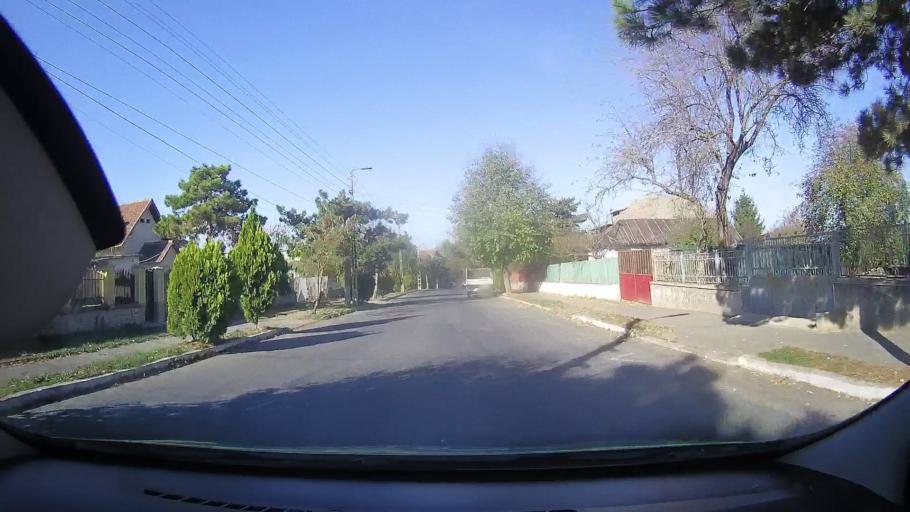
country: RO
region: Tulcea
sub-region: Oras Babadag
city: Babadag
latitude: 44.8900
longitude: 28.7287
